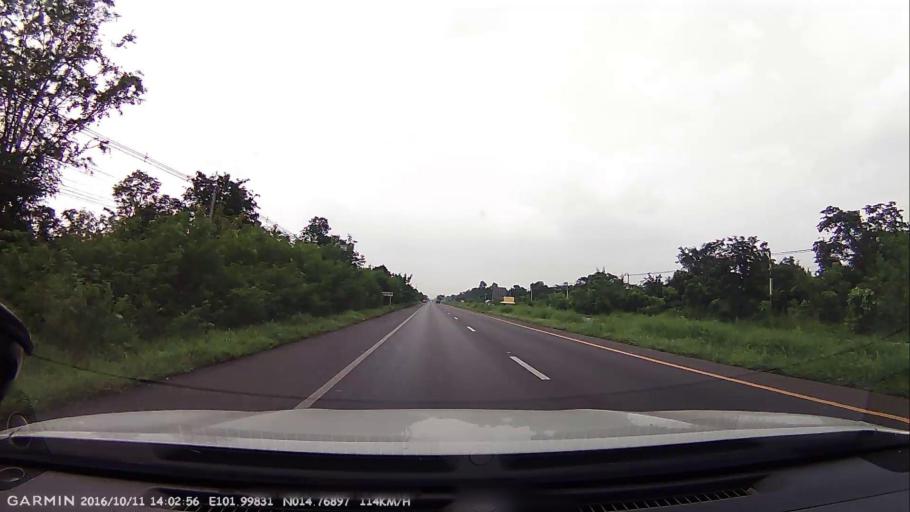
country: TH
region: Nakhon Ratchasima
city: Pak Thong Chai
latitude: 14.7689
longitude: 101.9985
